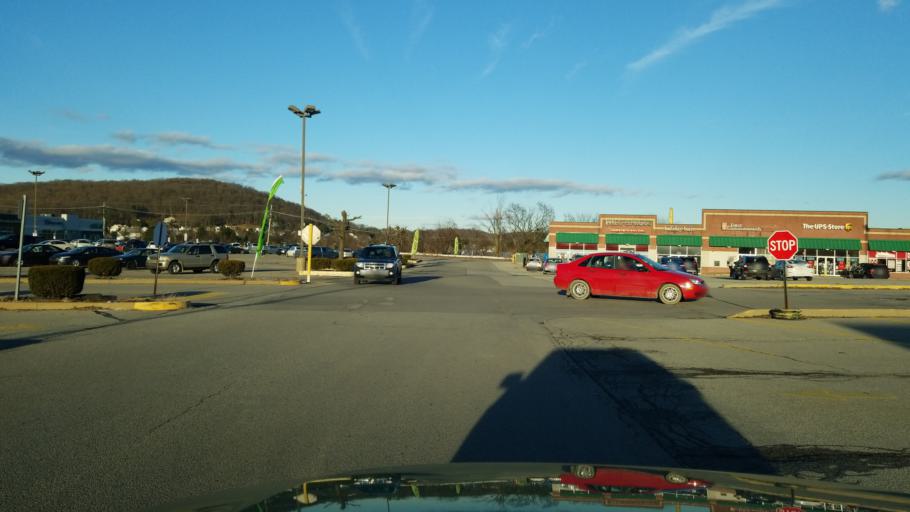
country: US
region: Pennsylvania
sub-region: Indiana County
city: Indiana
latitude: 40.6153
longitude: -79.1725
